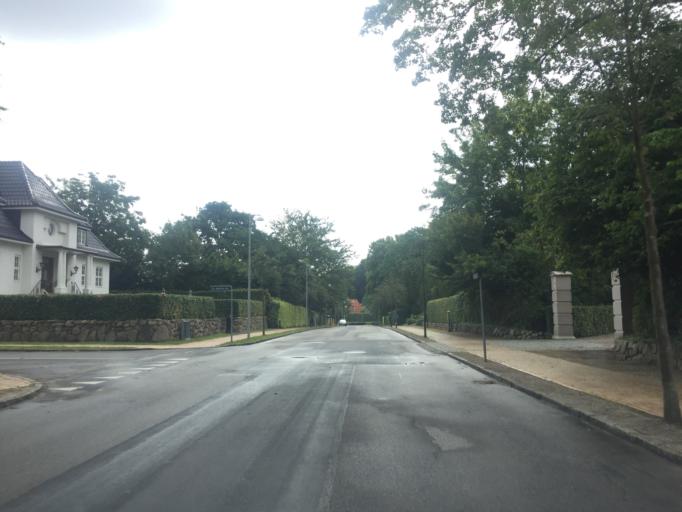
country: DK
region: South Denmark
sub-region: Odense Kommune
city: Odense
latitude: 55.3740
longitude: 10.3804
